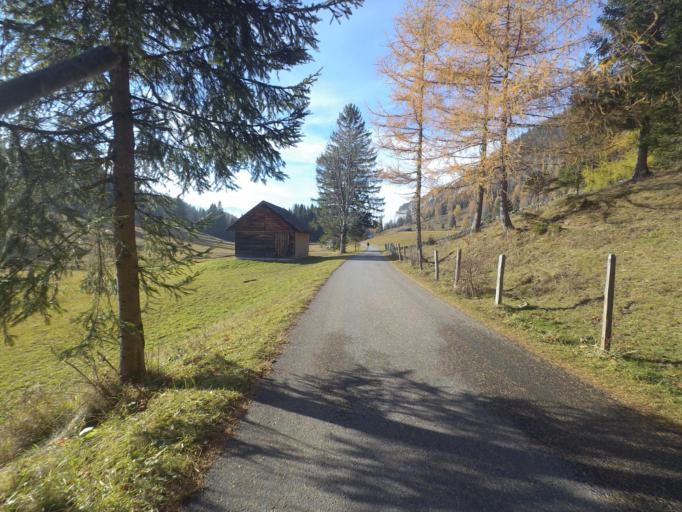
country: AT
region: Salzburg
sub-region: Politischer Bezirk Hallein
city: Scheffau am Tennengebirge
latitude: 47.6279
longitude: 13.2637
